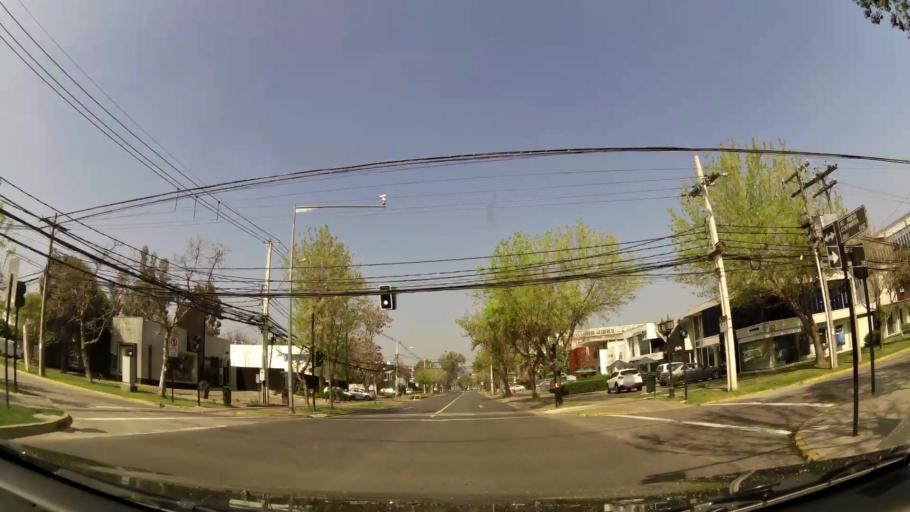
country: CL
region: Santiago Metropolitan
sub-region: Provincia de Santiago
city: Villa Presidente Frei, Nunoa, Santiago, Chile
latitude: -33.3968
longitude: -70.5976
